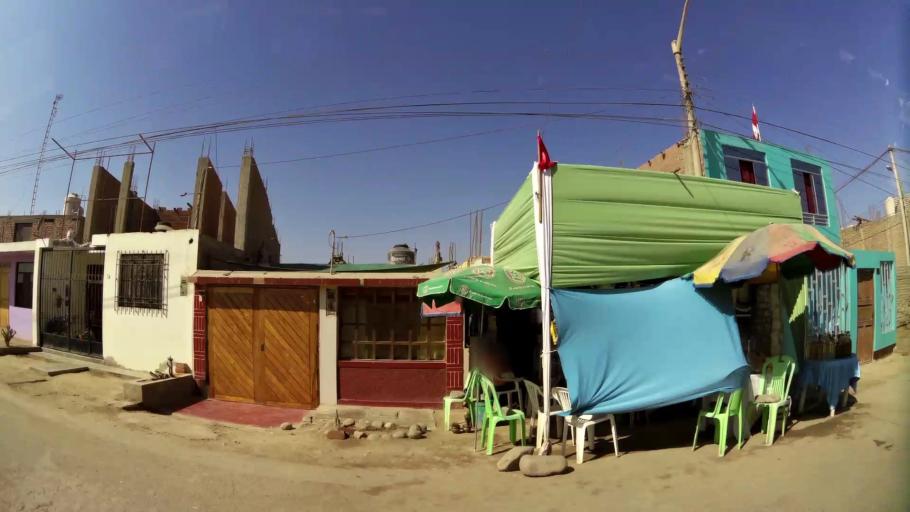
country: PE
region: Ica
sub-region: Provincia de Chincha
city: Sunampe
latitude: -13.4162
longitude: -76.1528
